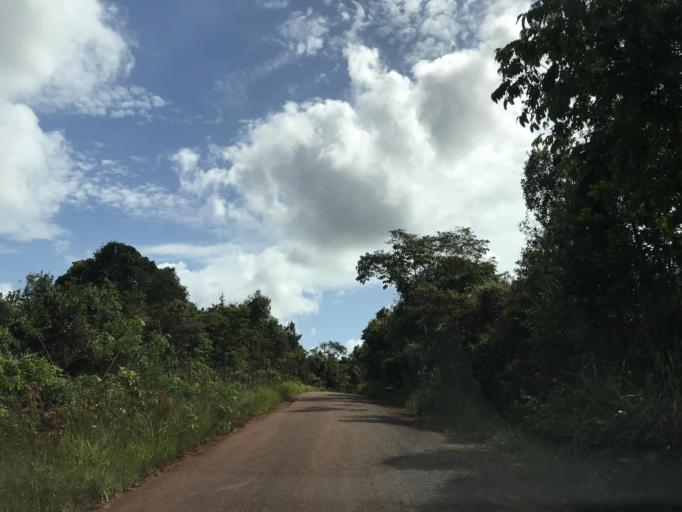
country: BR
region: Bahia
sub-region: Entre Rios
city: Entre Rios
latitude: -12.1716
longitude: -38.1111
